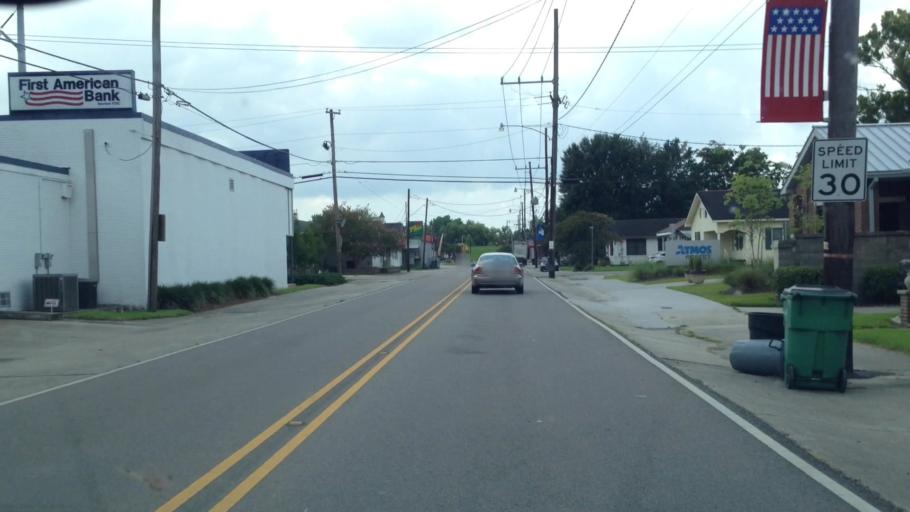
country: US
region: Louisiana
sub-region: Saint Charles Parish
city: Norco
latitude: 29.9995
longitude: -90.4126
